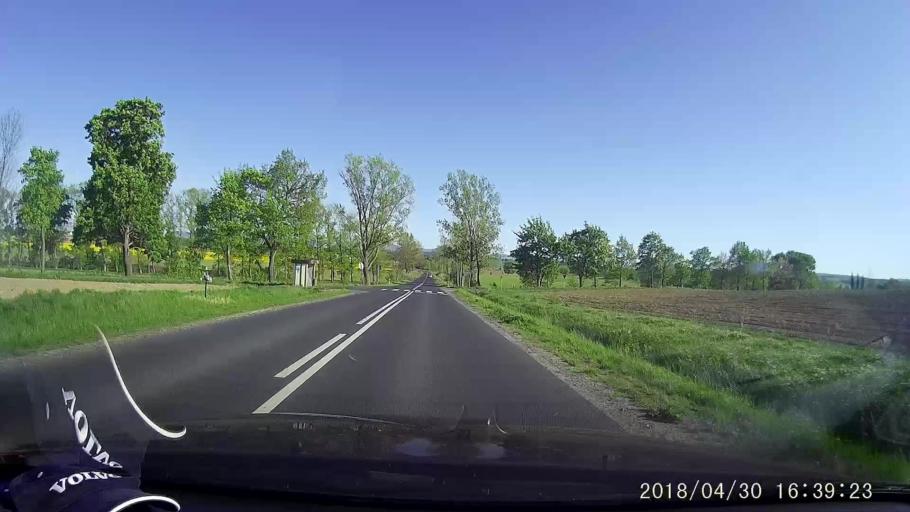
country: PL
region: Silesian Voivodeship
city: Zawidow
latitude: 51.0417
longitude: 15.0460
